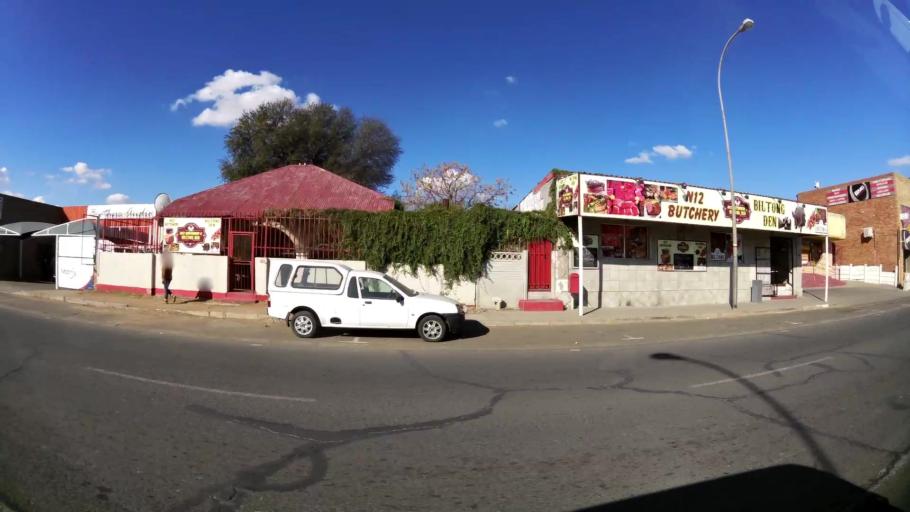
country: ZA
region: Northern Cape
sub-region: Frances Baard District Municipality
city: Kimberley
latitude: -28.7325
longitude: 24.7640
